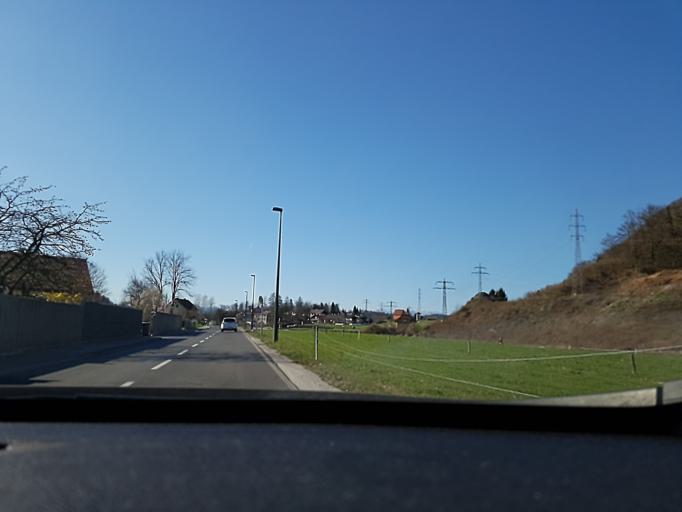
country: SI
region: Medvode
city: Zgornje Pirnice
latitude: 46.1213
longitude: 14.4479
